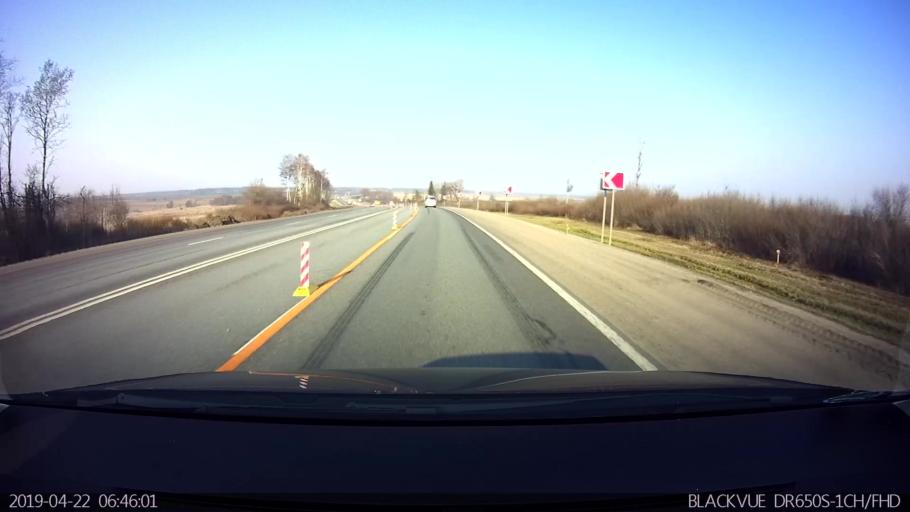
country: RU
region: Smolensk
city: Gagarin
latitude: 55.5058
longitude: 35.1196
